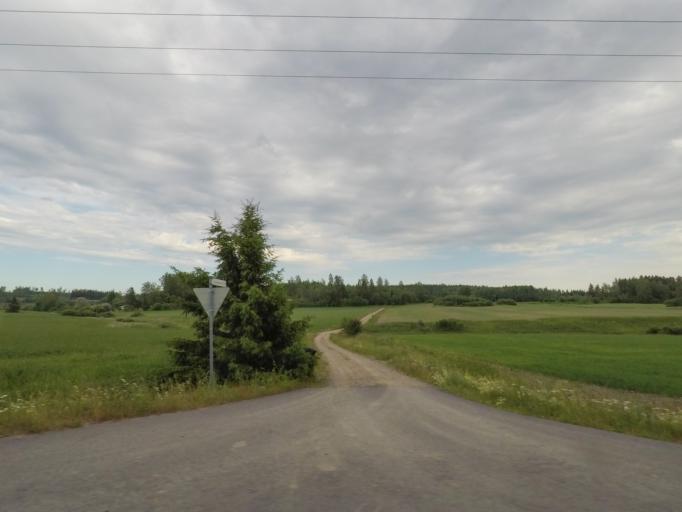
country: FI
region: Uusimaa
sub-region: Helsinki
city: Maentsaelae
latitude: 60.6905
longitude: 25.3763
